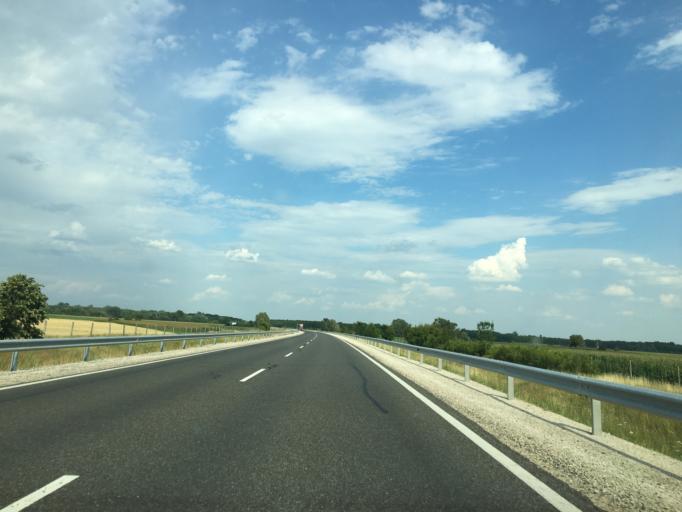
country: HU
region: Tolna
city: Bogyiszlo
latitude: 46.3514
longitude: 18.8675
